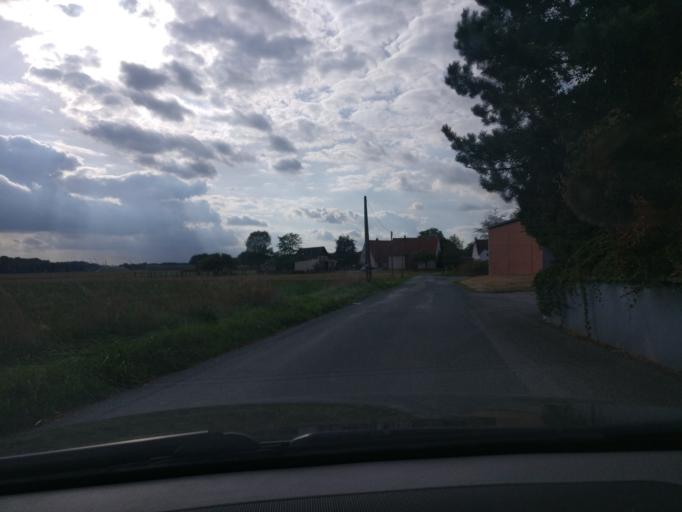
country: DE
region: Lower Saxony
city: Neuenkirchen
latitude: 52.1719
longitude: 8.3671
